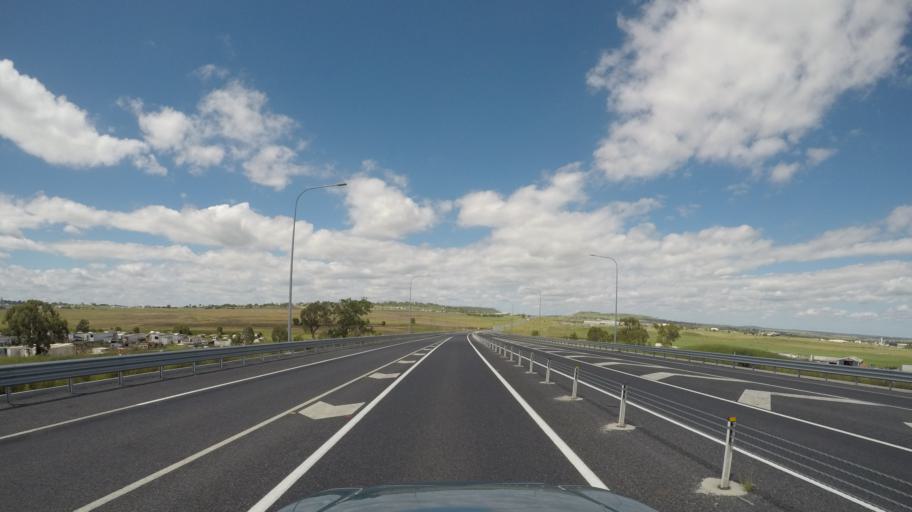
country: AU
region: Queensland
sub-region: Toowoomba
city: Wilsonton Heights
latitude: -27.5294
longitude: 151.8579
